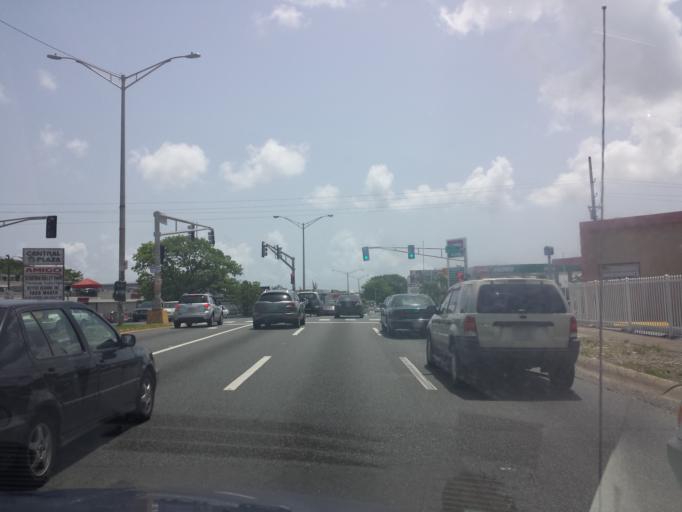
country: PR
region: Guaynabo
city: Guaynabo
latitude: 18.3989
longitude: -66.0975
